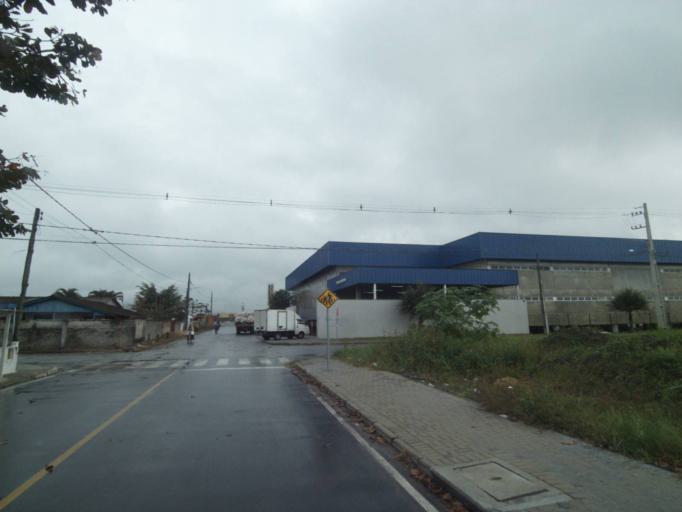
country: BR
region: Parana
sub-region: Paranagua
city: Paranagua
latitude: -25.5723
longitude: -48.5739
